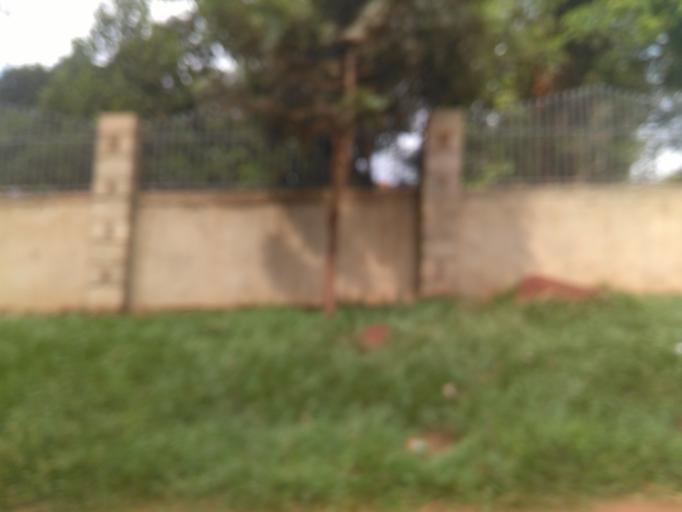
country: UG
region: Eastern Region
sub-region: Jinja District
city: Jinja
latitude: 0.4347
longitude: 33.2033
